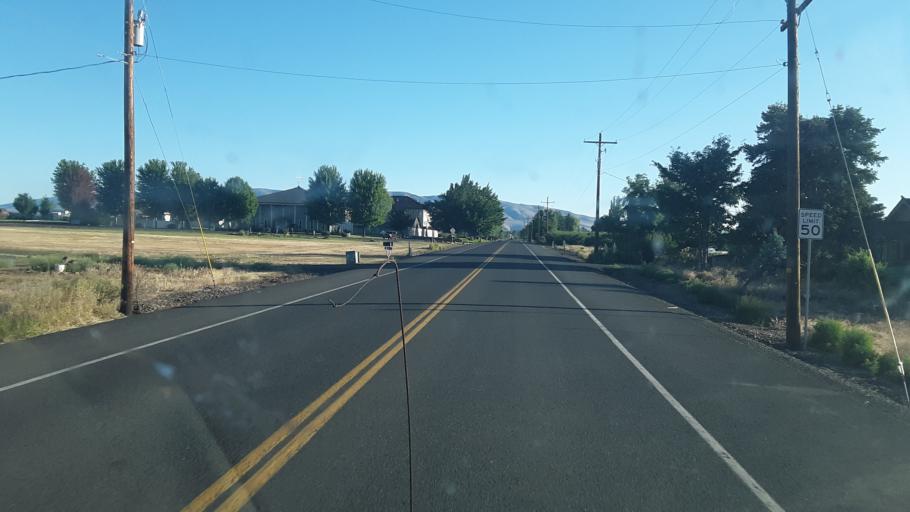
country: US
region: Washington
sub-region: Yakima County
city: Tieton
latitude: 46.6549
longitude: -120.7098
